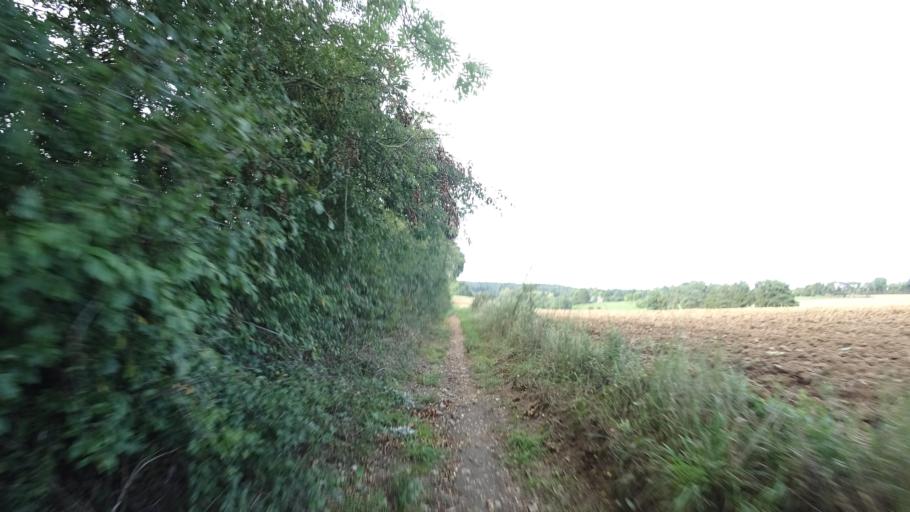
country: BE
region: Wallonia
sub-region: Province du Brabant Wallon
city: Genappe
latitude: 50.6289
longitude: 4.5023
